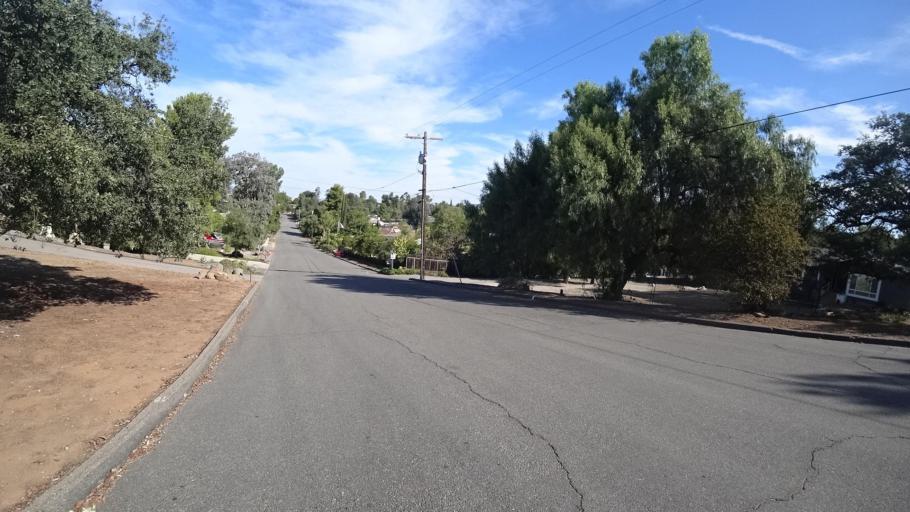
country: US
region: California
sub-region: San Diego County
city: Alpine
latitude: 32.8162
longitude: -116.7940
